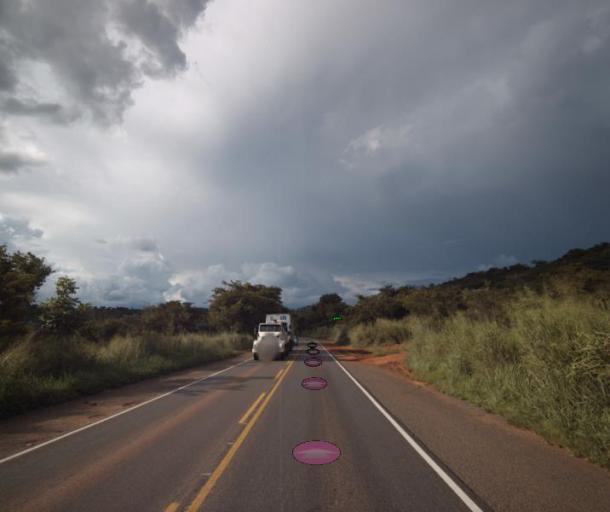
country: BR
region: Goias
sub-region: Rialma
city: Rialma
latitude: -15.2629
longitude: -49.5473
